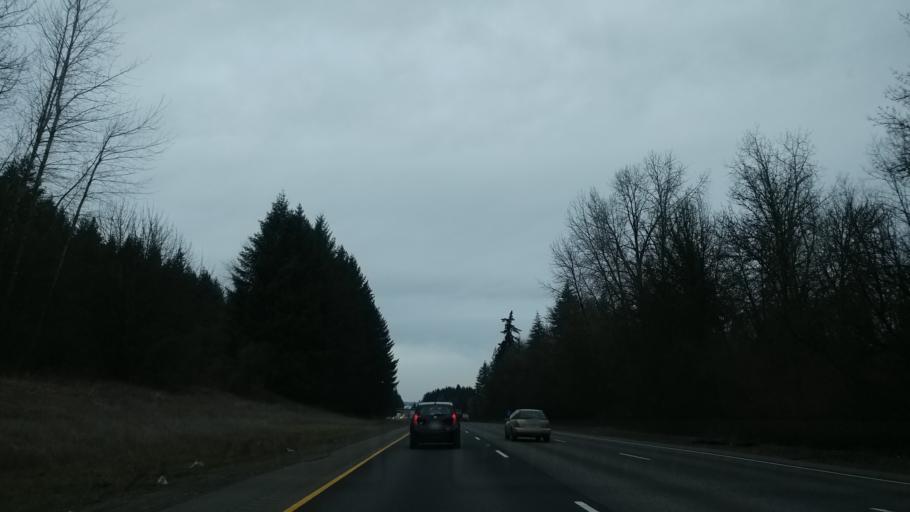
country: US
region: Washington
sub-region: Clark County
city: Mount Vista
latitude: 45.7877
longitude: -122.6741
